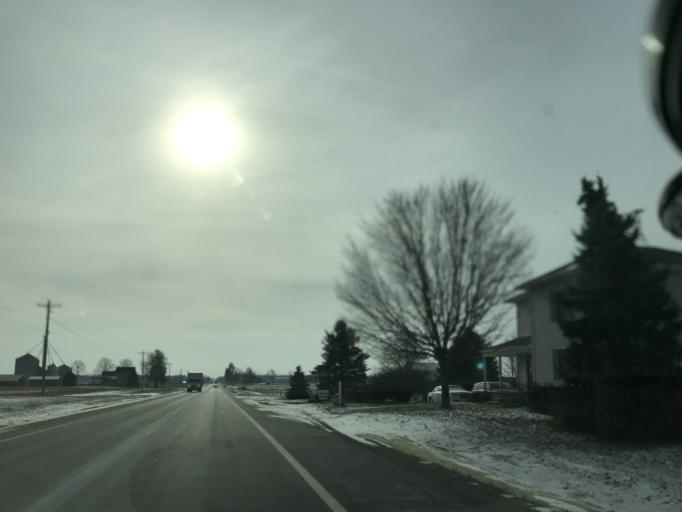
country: US
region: Michigan
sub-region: Ionia County
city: Lake Odessa
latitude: 42.8277
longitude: -85.0748
